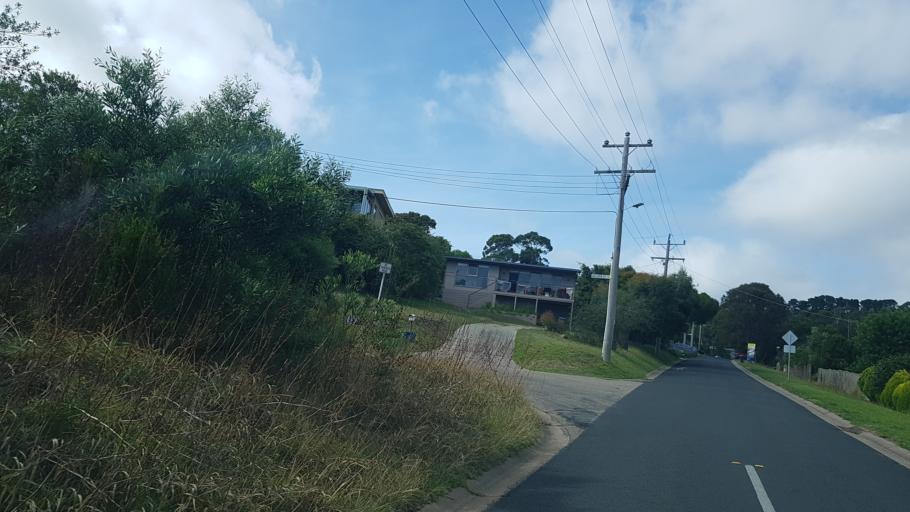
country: AU
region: Victoria
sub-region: Mornington Peninsula
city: Dromana
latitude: -38.3456
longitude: 144.9757
